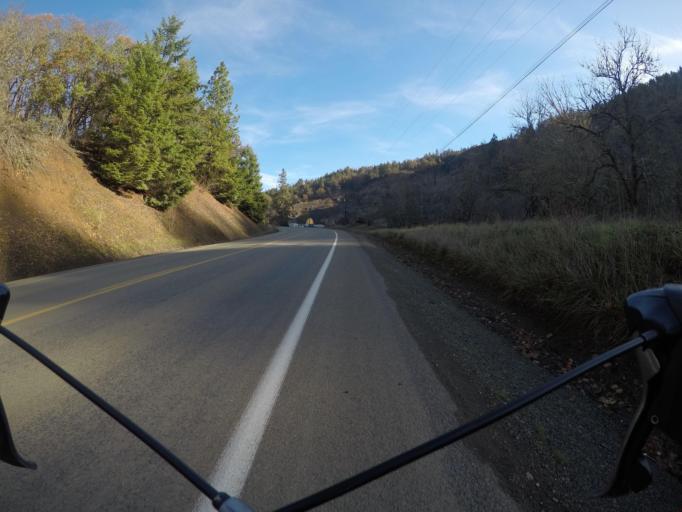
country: US
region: Oregon
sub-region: Douglas County
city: Winston
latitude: 43.1883
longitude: -123.4452
